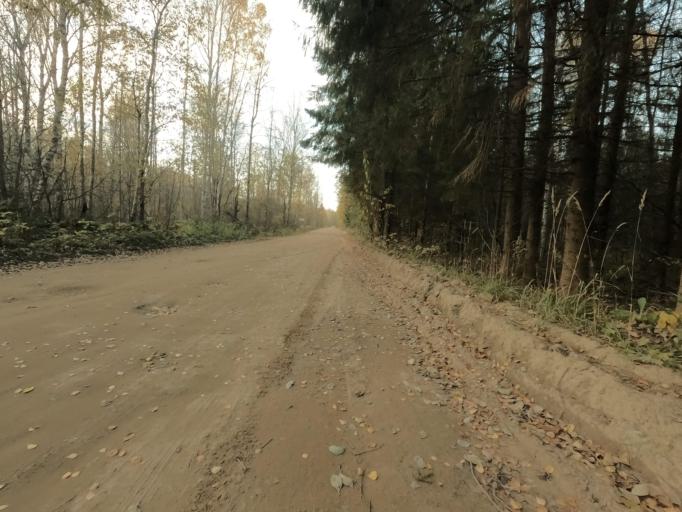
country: RU
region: Leningrad
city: Priladozhskiy
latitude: 59.7461
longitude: 31.3061
